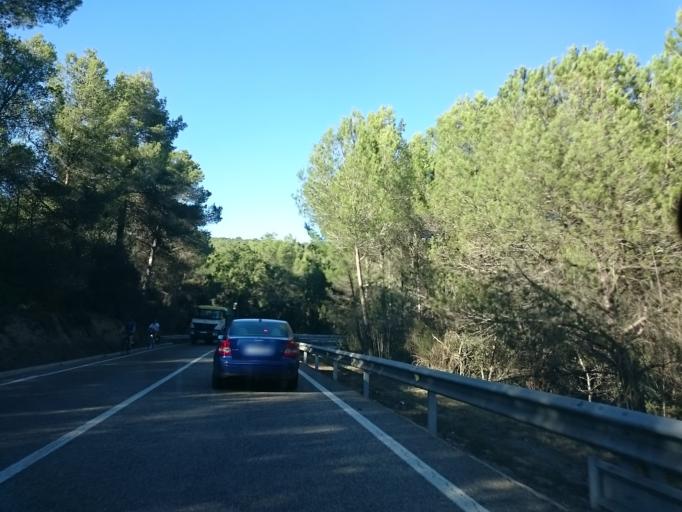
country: ES
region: Catalonia
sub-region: Provincia de Barcelona
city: Piera
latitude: 41.5355
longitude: 1.7356
